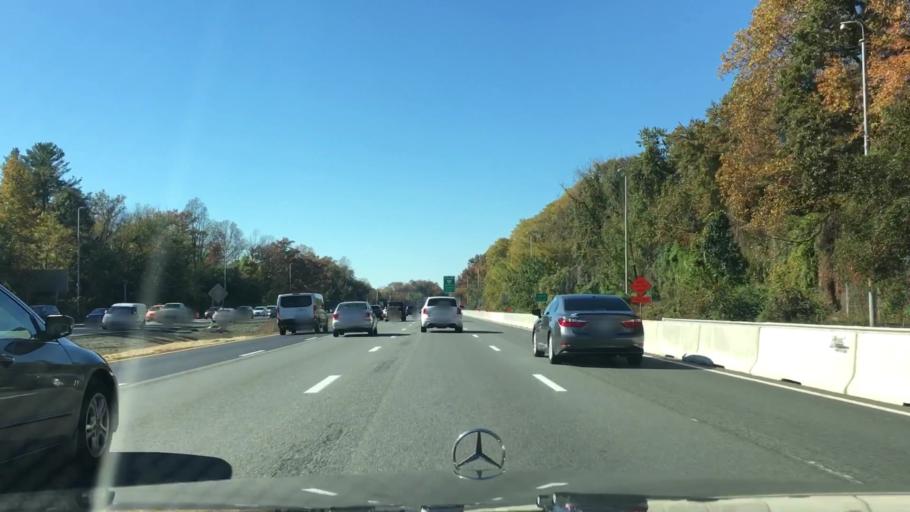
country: US
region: Virginia
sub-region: Fairfax County
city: Oakton
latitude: 38.8716
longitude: -77.2818
